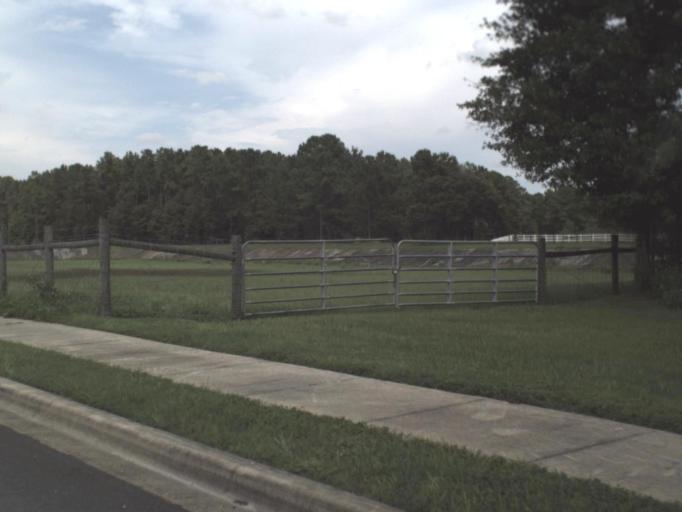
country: US
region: Florida
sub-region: Hernando County
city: Masaryktown
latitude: 28.4679
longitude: -82.4428
